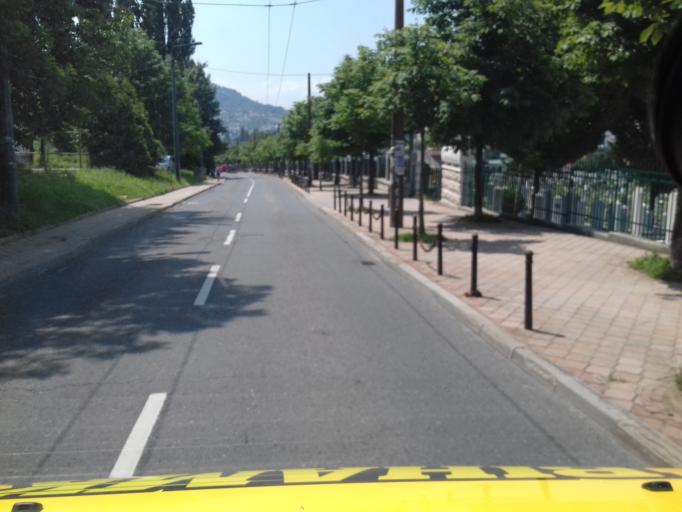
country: BA
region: Federation of Bosnia and Herzegovina
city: Kobilja Glava
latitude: 43.8696
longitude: 18.4120
